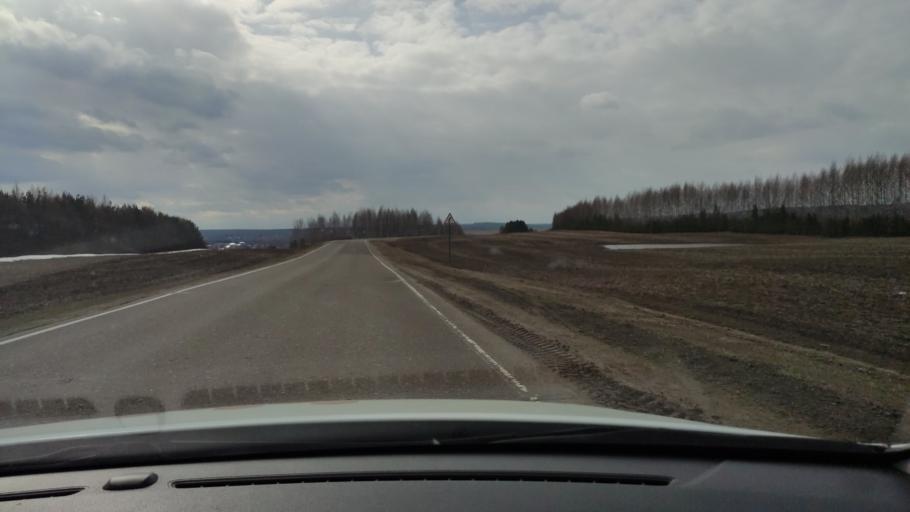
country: RU
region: Tatarstan
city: Vysokaya Gora
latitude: 56.1984
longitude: 49.2266
